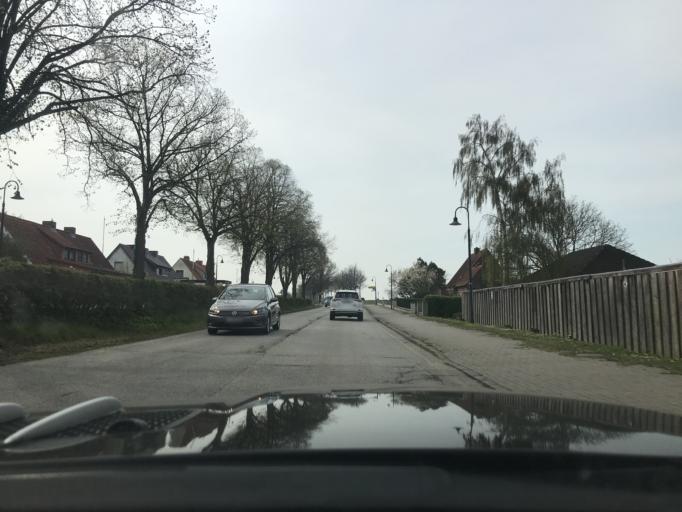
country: DE
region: Schleswig-Holstein
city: Heringsdorf
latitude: 54.2997
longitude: 11.0113
